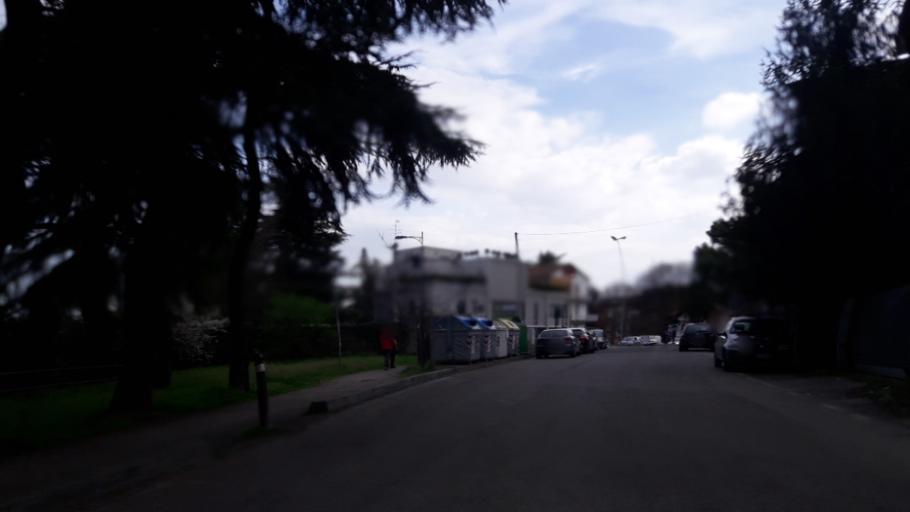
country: IT
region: Emilia-Romagna
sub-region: Provincia di Reggio Emilia
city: Reggio nell'Emilia
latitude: 44.6841
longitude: 10.6223
